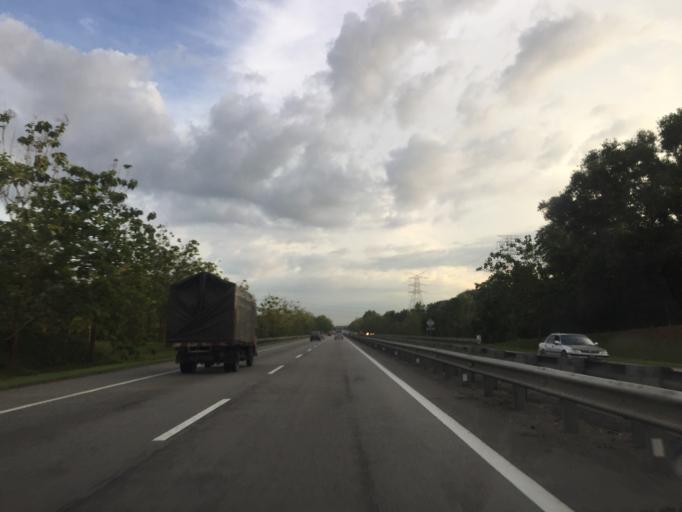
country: MY
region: Kedah
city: Gurun
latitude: 5.7816
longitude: 100.5026
